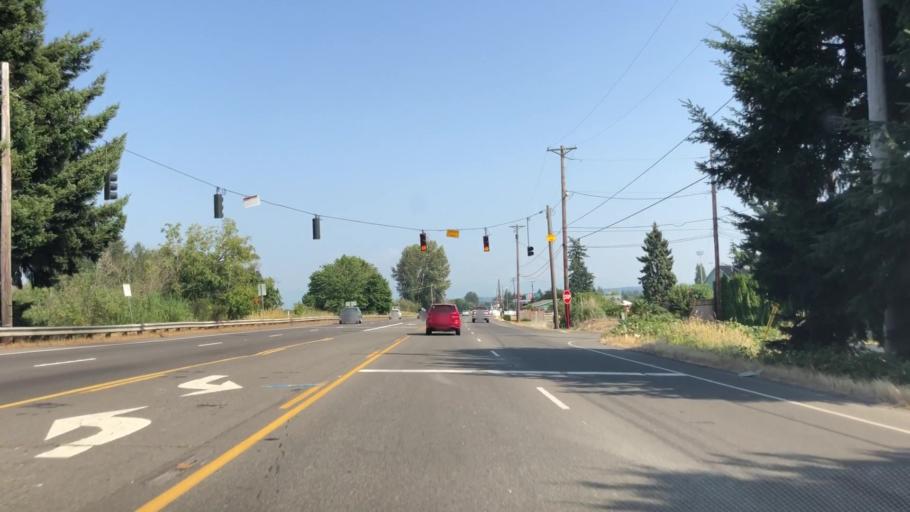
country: US
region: Washington
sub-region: Pierce County
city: Fife
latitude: 47.2213
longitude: -122.3558
